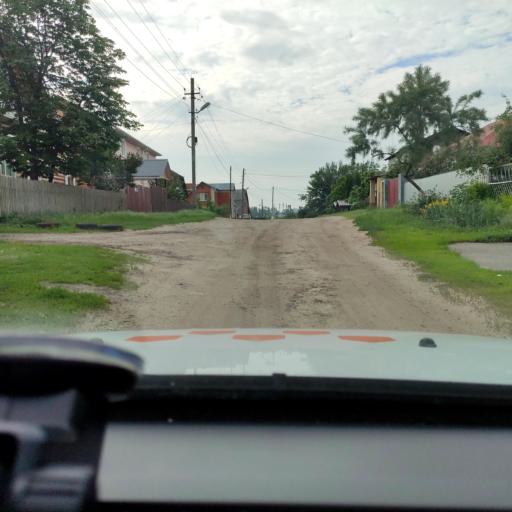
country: RU
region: Voronezj
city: Maslovka
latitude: 51.5799
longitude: 39.3083
